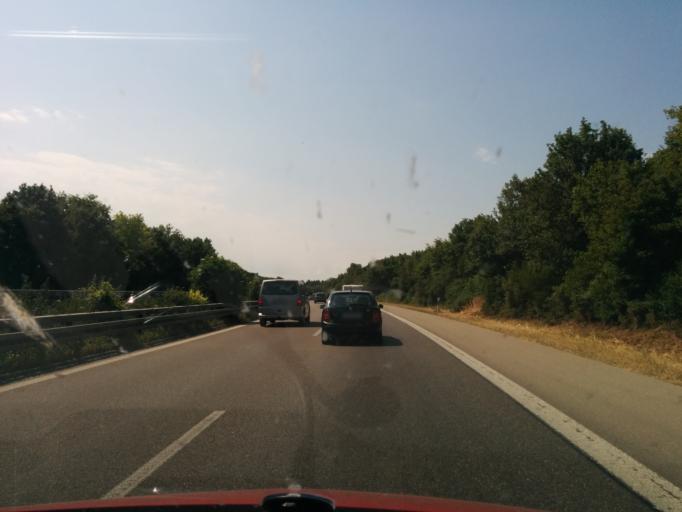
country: DE
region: Bavaria
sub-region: Swabia
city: Oberottmarshausen
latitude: 48.2304
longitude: 10.8665
